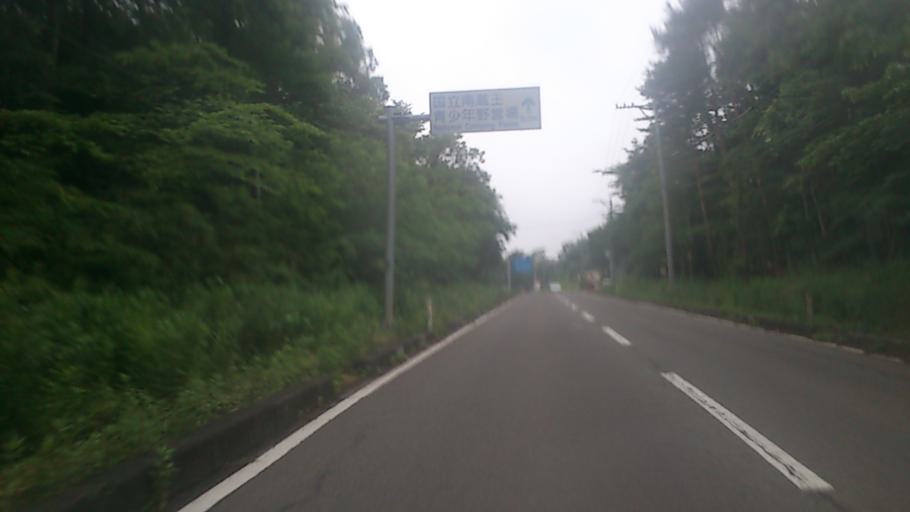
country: JP
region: Miyagi
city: Shiroishi
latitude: 38.1143
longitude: 140.5671
